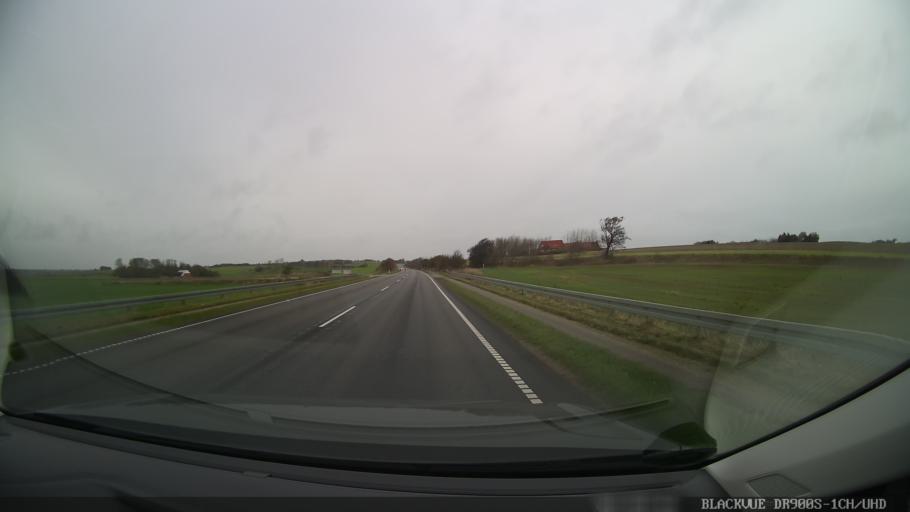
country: DK
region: North Denmark
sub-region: Thisted Kommune
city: Thisted
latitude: 56.8664
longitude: 8.6816
